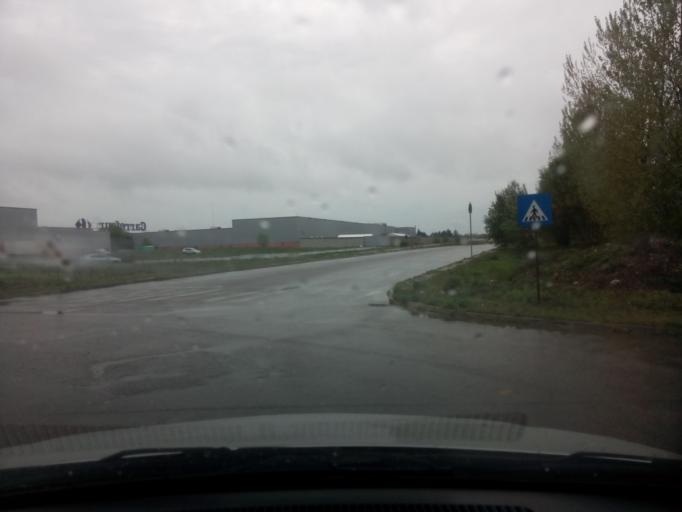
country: RO
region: Ilfov
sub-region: Comuna Otopeni
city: Otopeni
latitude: 44.5088
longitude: 26.0916
